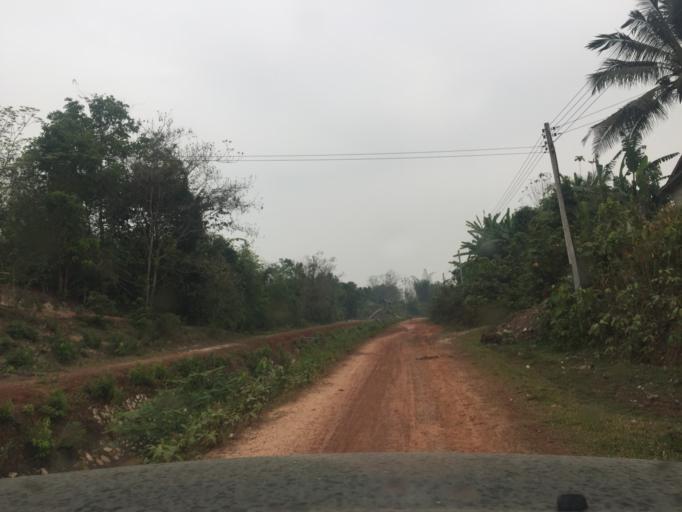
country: LA
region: Xiagnabouli
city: Sainyabuli
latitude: 18.9822
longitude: 101.4820
